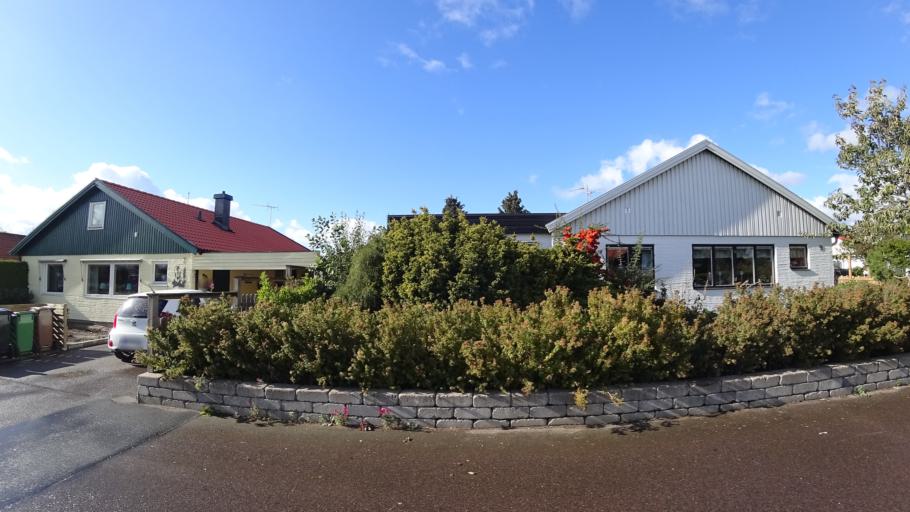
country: SE
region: Skane
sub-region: Kavlinge Kommun
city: Loddekopinge
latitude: 55.7551
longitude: 13.0045
